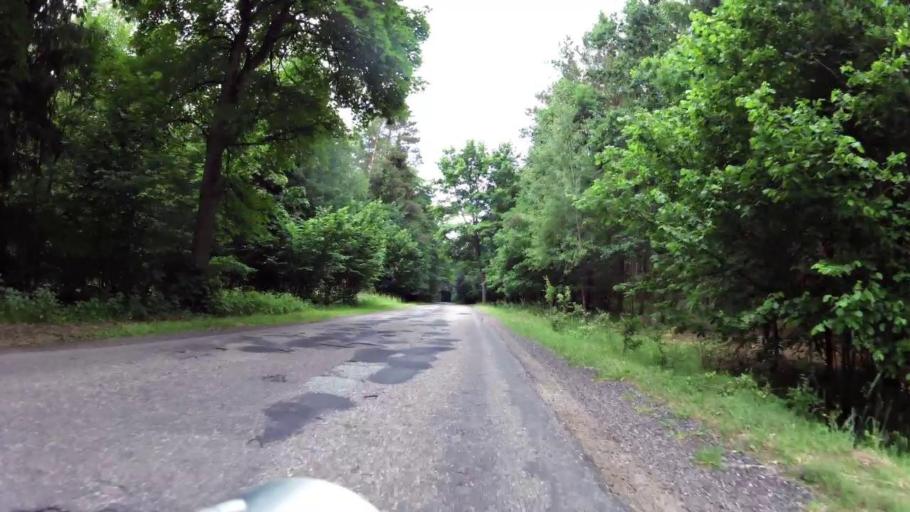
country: PL
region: West Pomeranian Voivodeship
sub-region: Powiat szczecinecki
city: Bialy Bor
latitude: 53.9632
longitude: 16.7301
